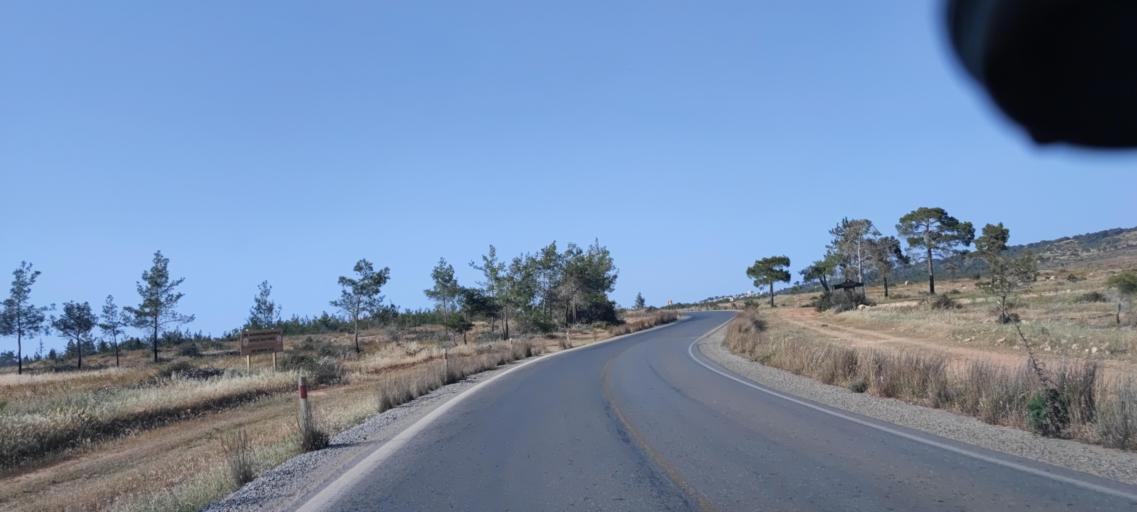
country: CY
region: Lefkosia
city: Morfou
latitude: 35.2803
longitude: 33.0404
